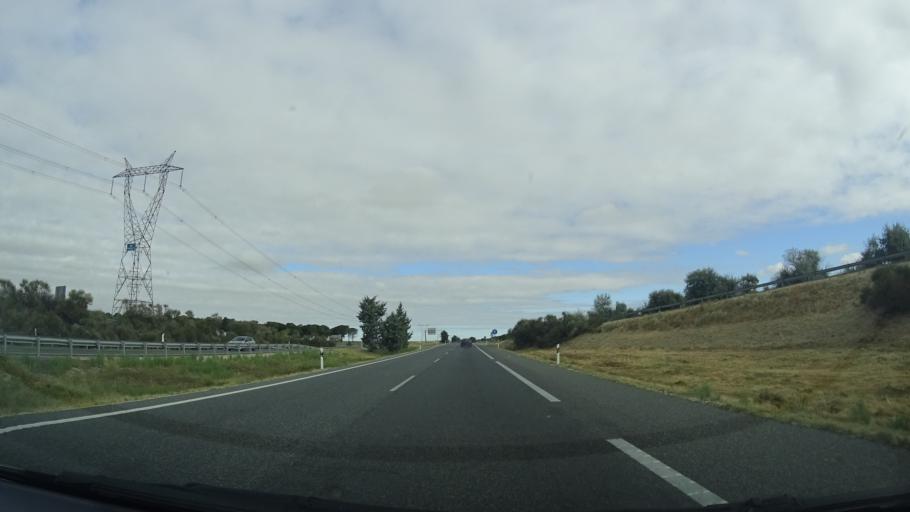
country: ES
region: Castille and Leon
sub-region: Provincia de Valladolid
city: San Pablo de la Moraleja
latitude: 41.1498
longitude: -4.7892
